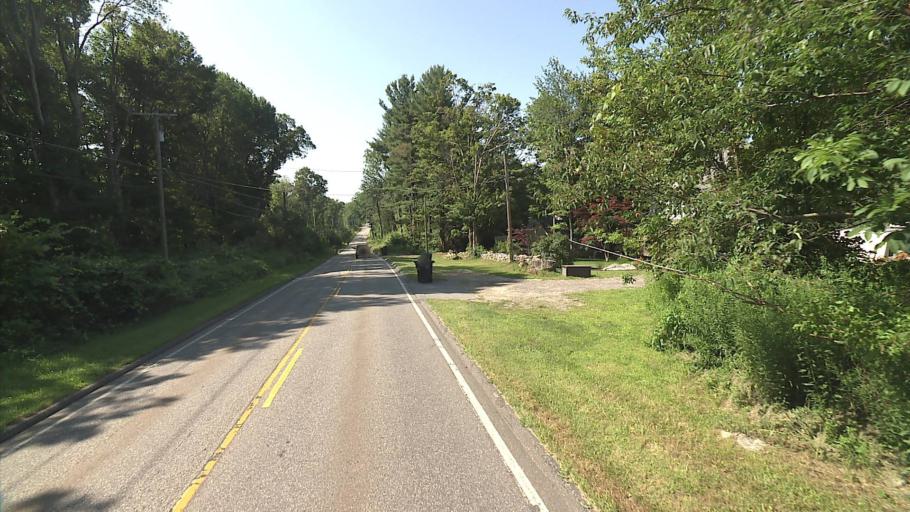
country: US
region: Connecticut
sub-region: Litchfield County
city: Torrington
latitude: 41.8449
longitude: -73.0748
